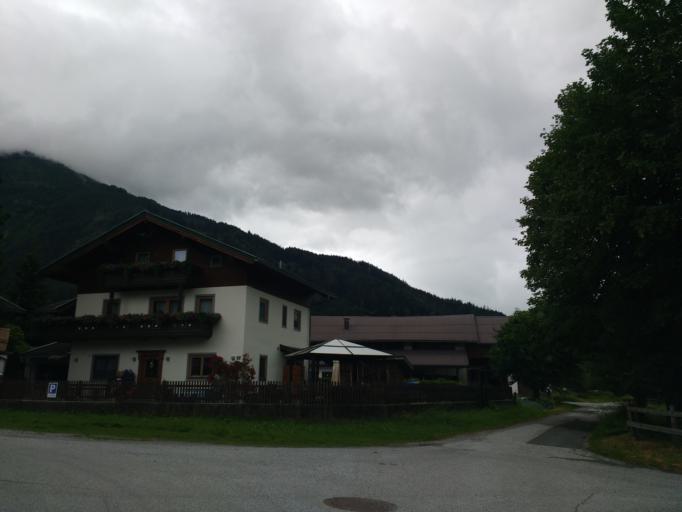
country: AT
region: Salzburg
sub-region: Politischer Bezirk Zell am See
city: Wald im Pinzgau
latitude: 47.2381
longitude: 12.2540
